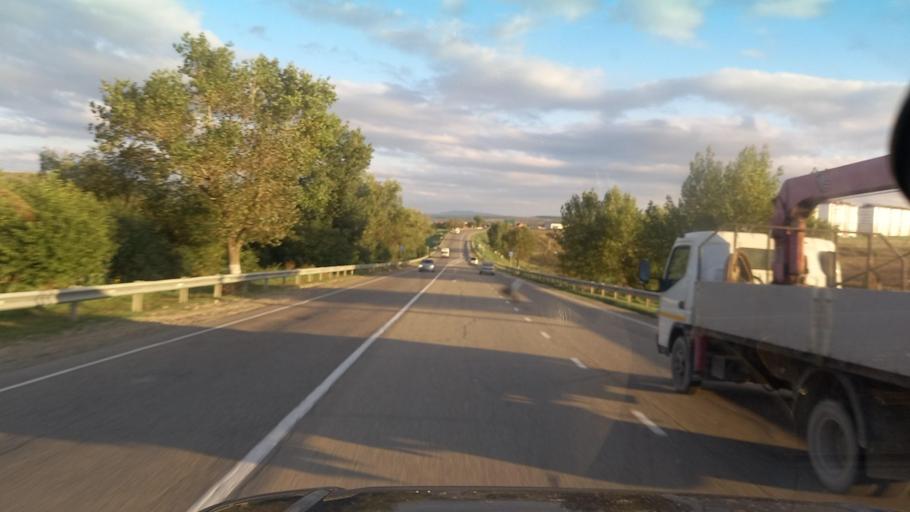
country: RU
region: Krasnodarskiy
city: Krymsk
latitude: 44.9293
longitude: 37.9658
